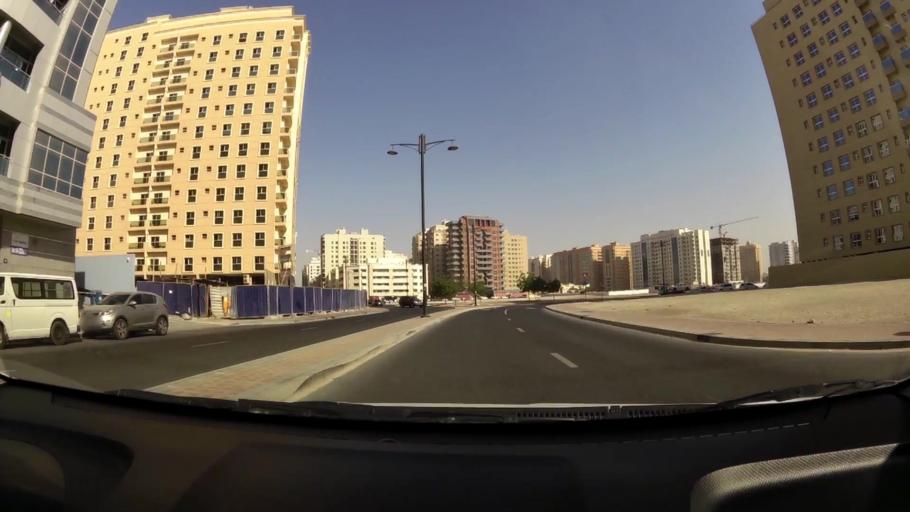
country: AE
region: Ash Shariqah
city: Sharjah
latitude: 25.2947
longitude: 55.3770
